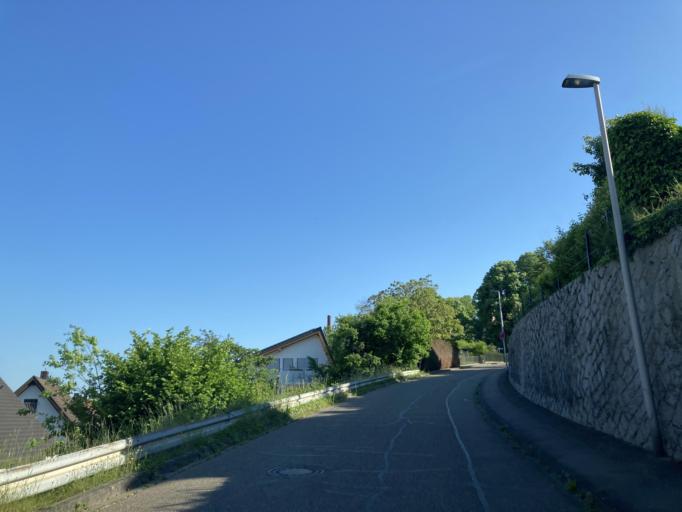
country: DE
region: Baden-Wuerttemberg
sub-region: Freiburg Region
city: Achern
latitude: 48.6175
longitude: 8.0872
